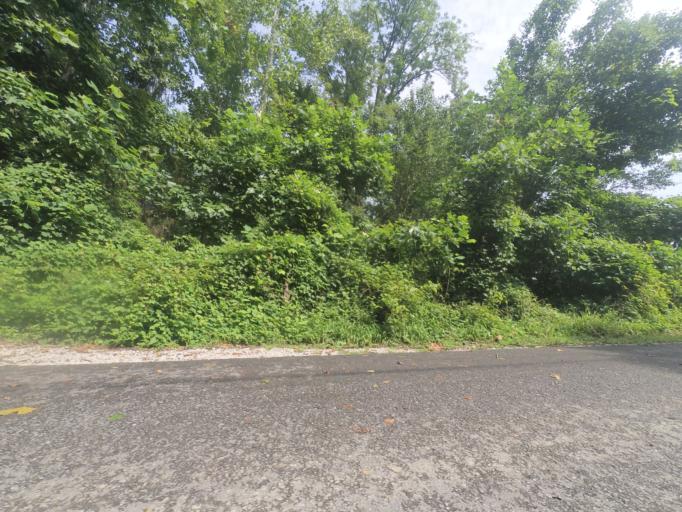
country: US
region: West Virginia
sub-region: Cabell County
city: Huntington
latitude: 38.4054
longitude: -82.4443
